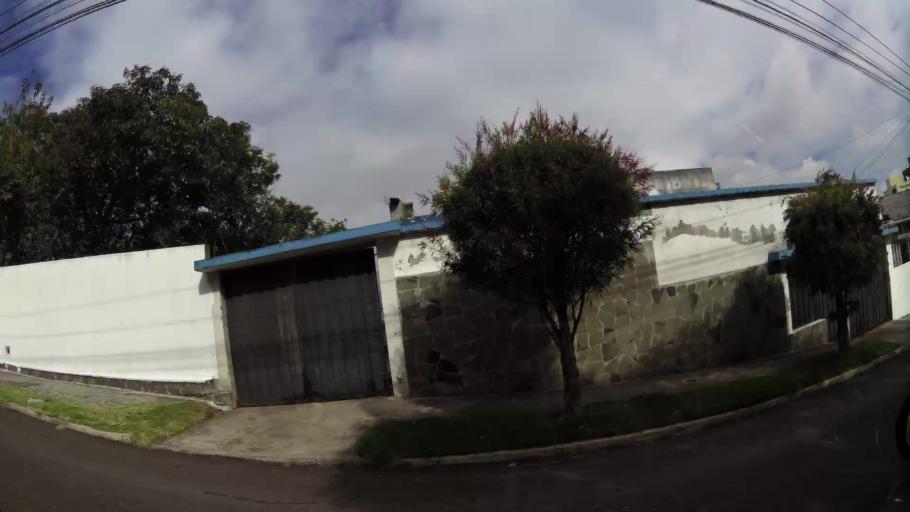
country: EC
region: Pichincha
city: Quito
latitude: -0.1813
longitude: -78.4740
